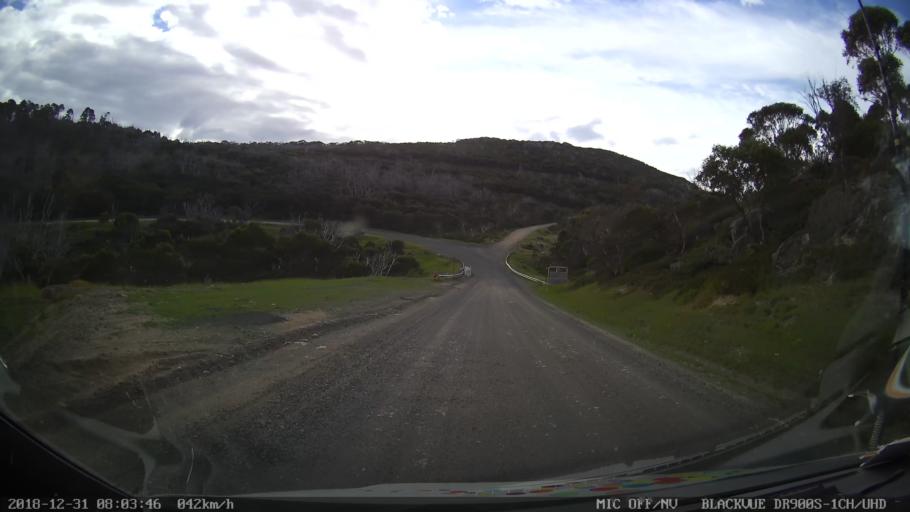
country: AU
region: New South Wales
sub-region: Snowy River
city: Jindabyne
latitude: -36.3657
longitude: 148.4041
